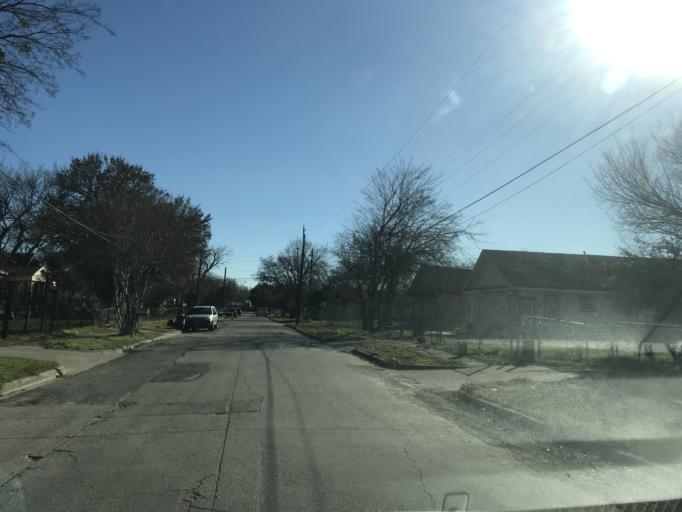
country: US
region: Texas
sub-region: Dallas County
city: Cockrell Hill
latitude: 32.7739
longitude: -96.9055
